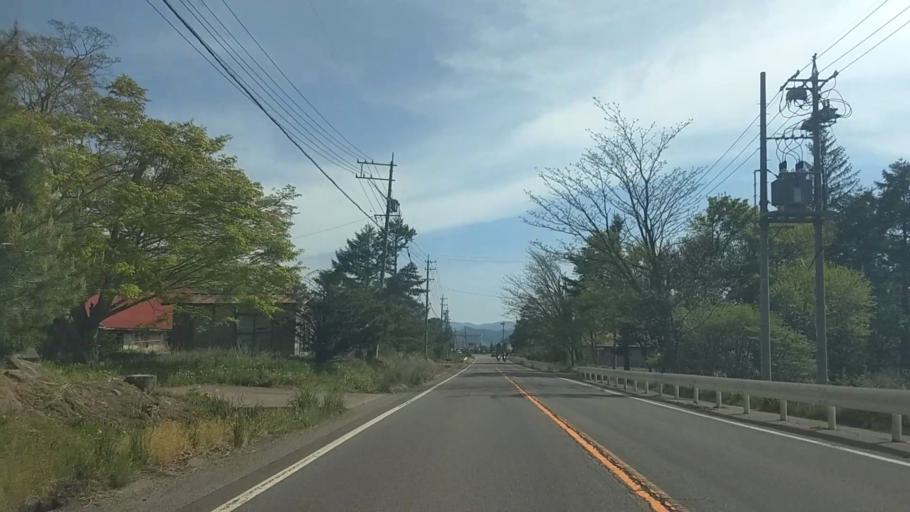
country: JP
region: Nagano
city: Saku
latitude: 35.9785
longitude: 138.4822
